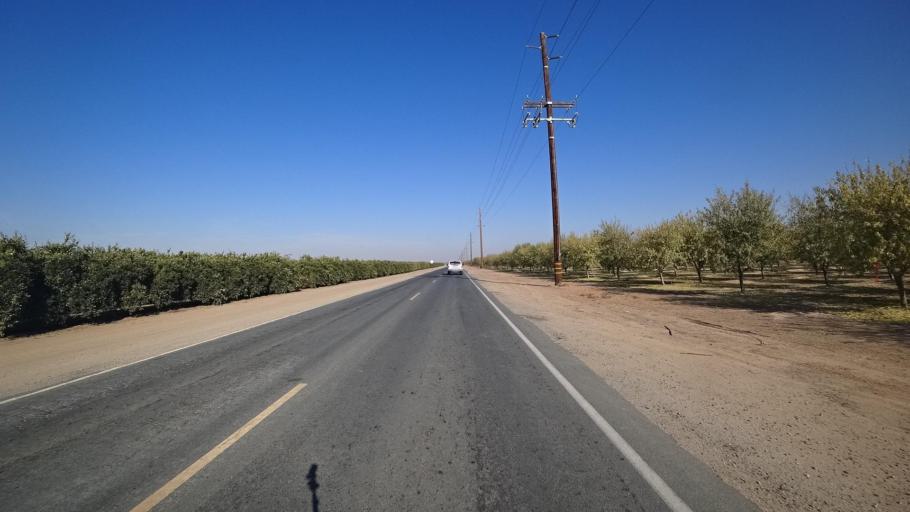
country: US
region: California
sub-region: Kern County
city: Delano
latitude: 35.7334
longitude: -119.2231
